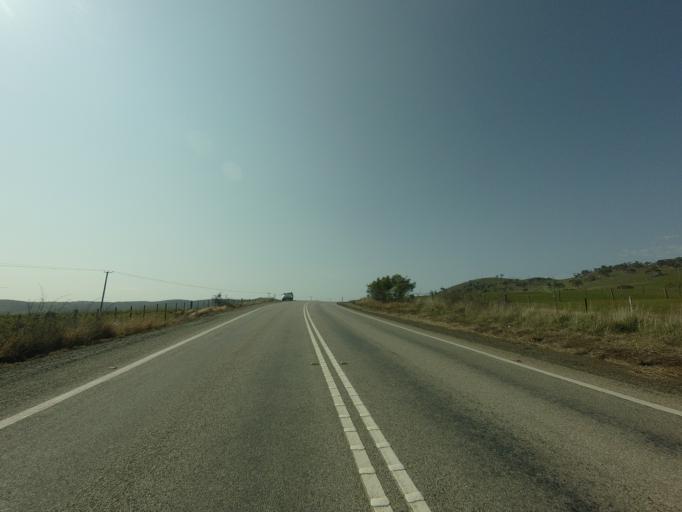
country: AU
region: Tasmania
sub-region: Northern Midlands
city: Evandale
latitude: -41.8223
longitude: 147.5248
